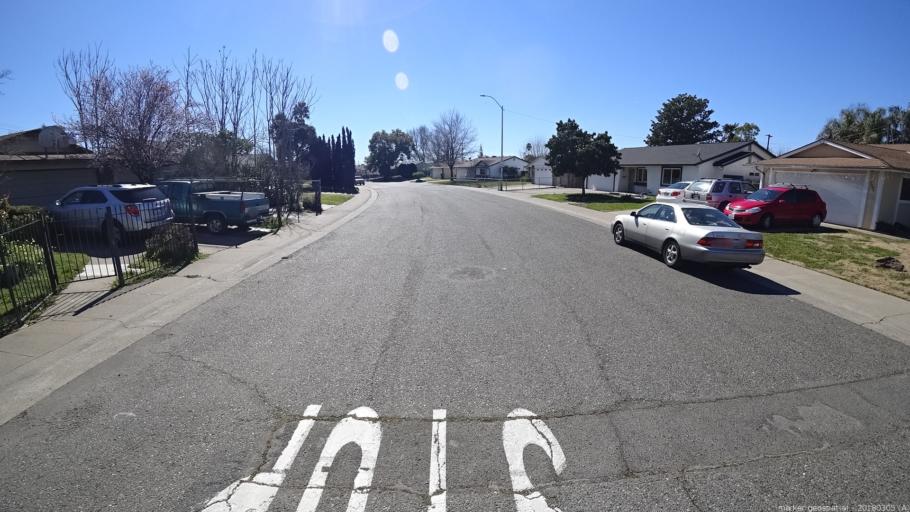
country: US
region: California
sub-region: Sacramento County
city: Florin
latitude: 38.4917
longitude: -121.3884
